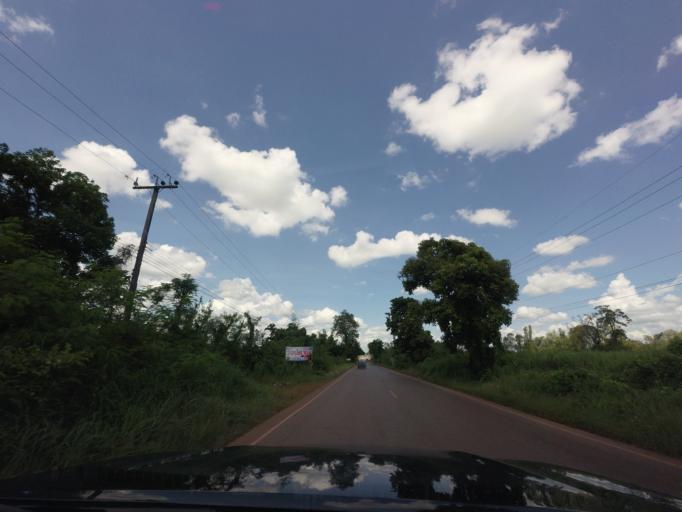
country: TH
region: Changwat Udon Thani
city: Ban Dung
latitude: 17.7416
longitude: 103.2592
